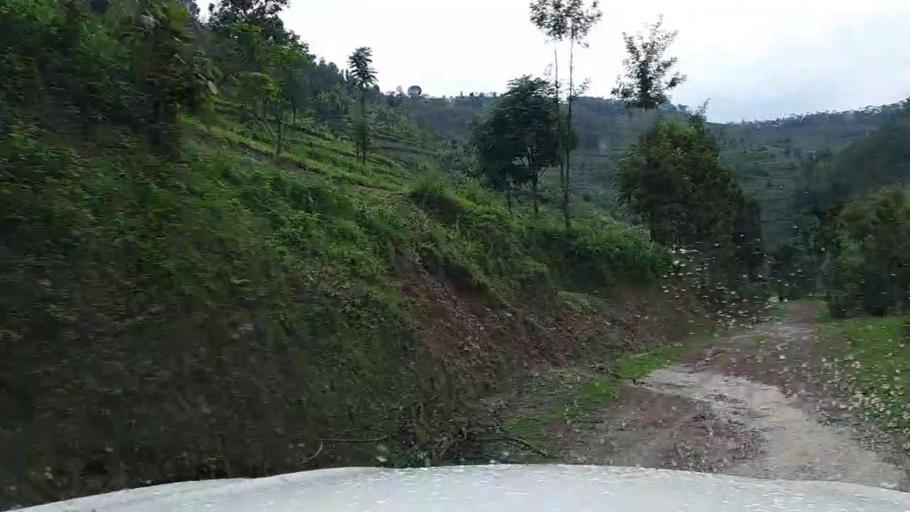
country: RW
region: Northern Province
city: Byumba
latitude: -1.7219
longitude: 29.9127
